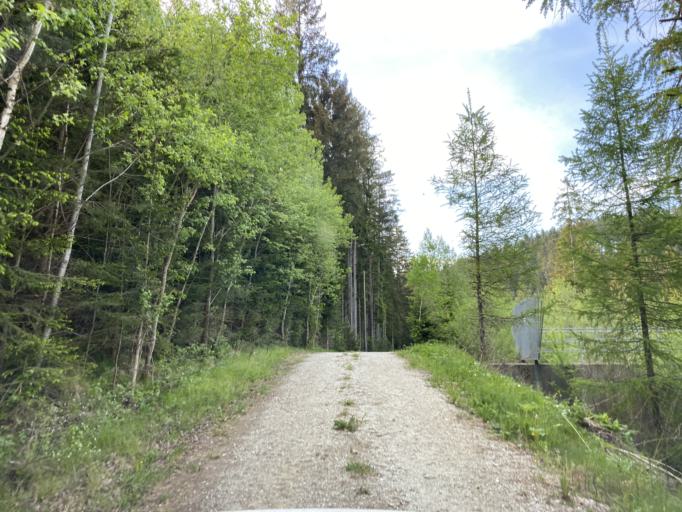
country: AT
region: Styria
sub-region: Politischer Bezirk Weiz
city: Birkfeld
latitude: 47.3601
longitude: 15.6803
